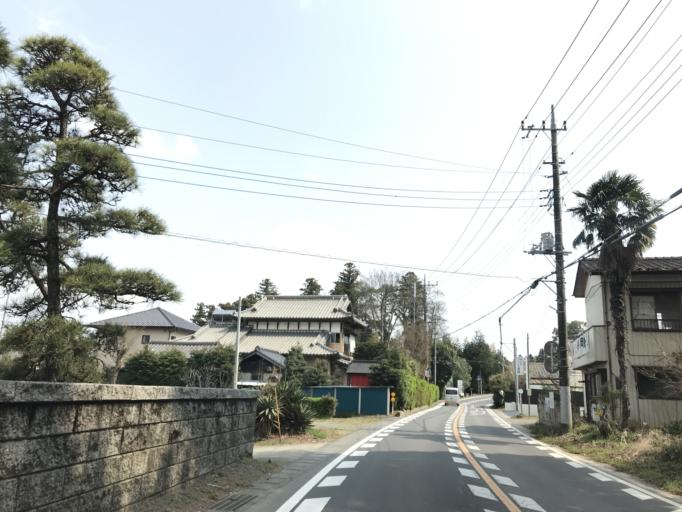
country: JP
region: Ibaraki
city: Ushiku
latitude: 36.0034
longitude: 140.0693
